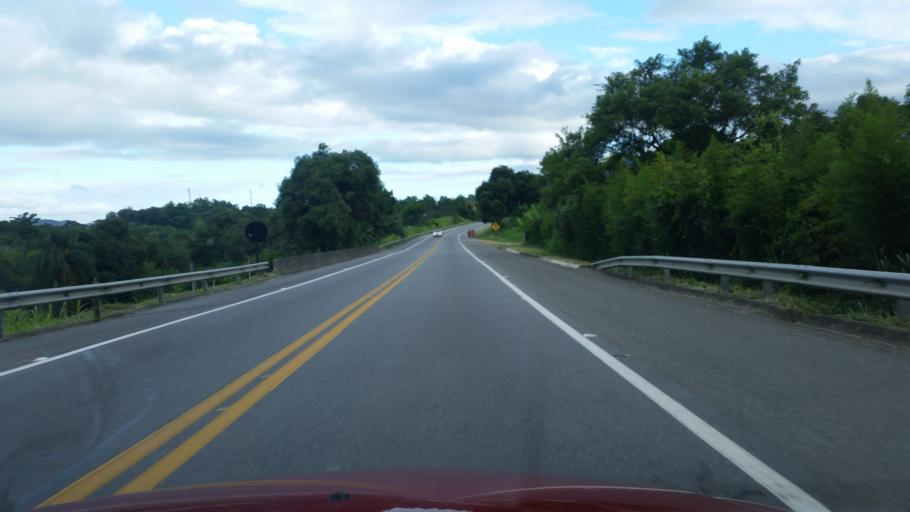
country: BR
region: Sao Paulo
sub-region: Miracatu
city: Miracatu
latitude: -24.2766
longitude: -47.2475
